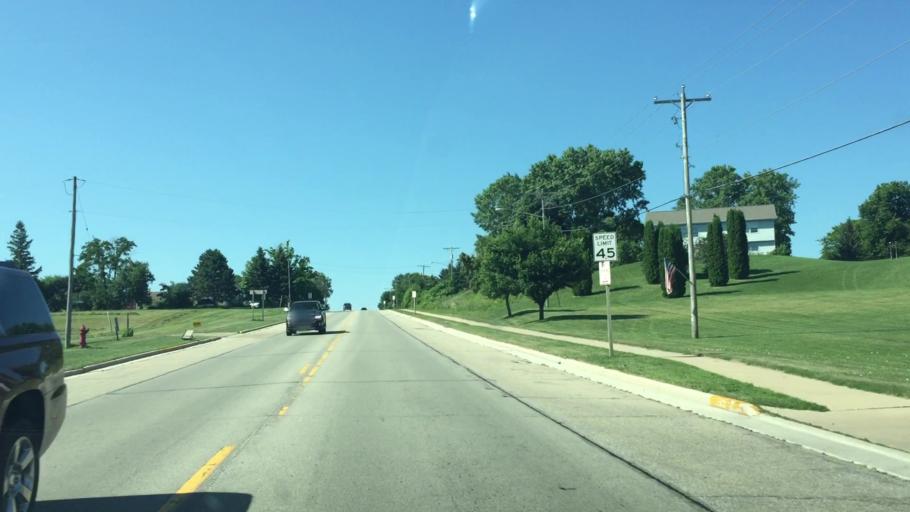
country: US
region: Wisconsin
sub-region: Calumet County
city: Sherwood
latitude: 44.1693
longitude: -88.2617
